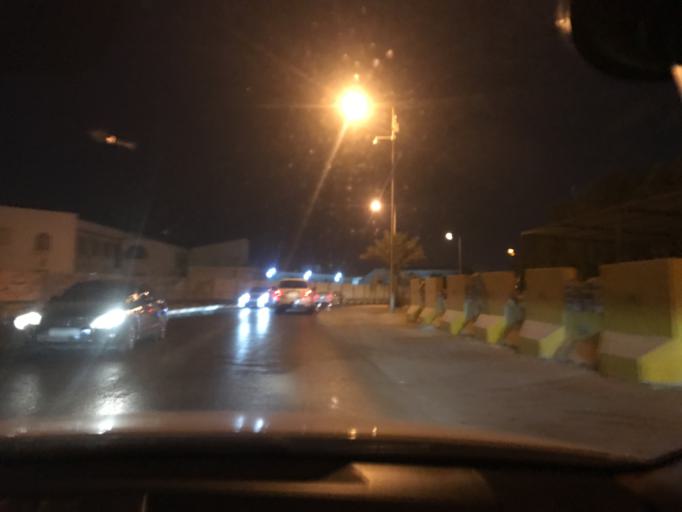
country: BH
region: Muharraq
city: Al Muharraq
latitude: 26.2812
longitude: 50.6263
